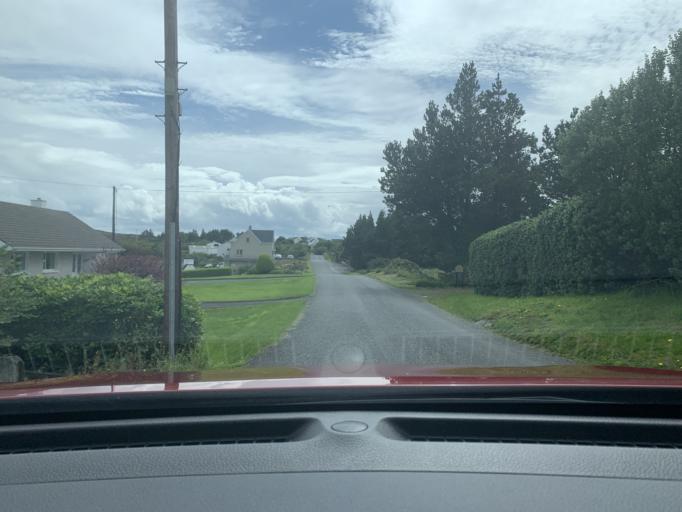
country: IE
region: Ulster
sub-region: County Donegal
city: Dungloe
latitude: 54.9435
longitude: -8.3582
